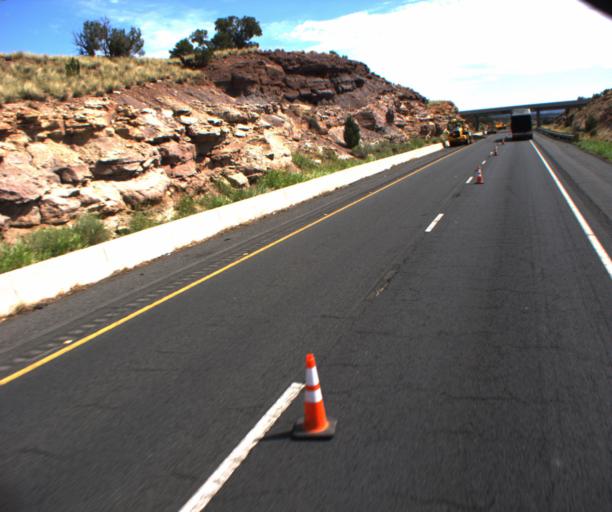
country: US
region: Arizona
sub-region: Apache County
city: Houck
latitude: 35.2573
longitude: -109.2790
